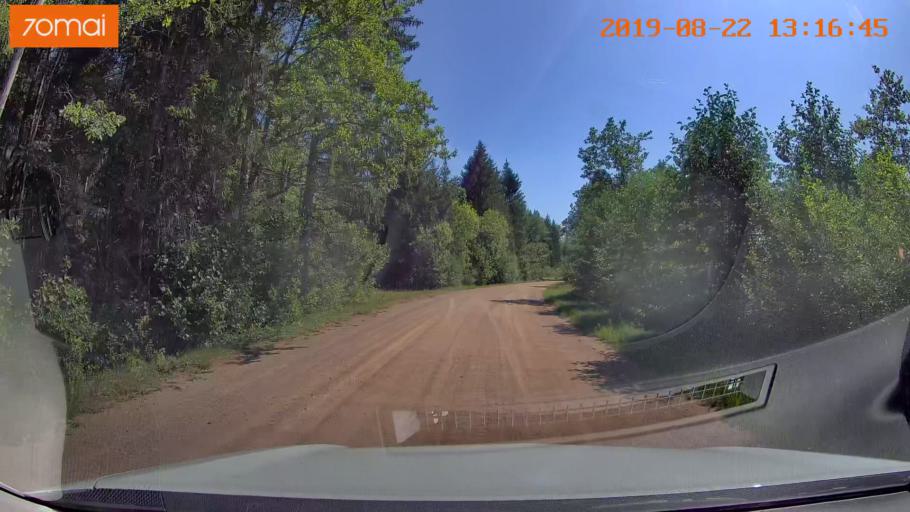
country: BY
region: Minsk
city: Prawdzinski
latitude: 53.2536
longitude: 27.9145
